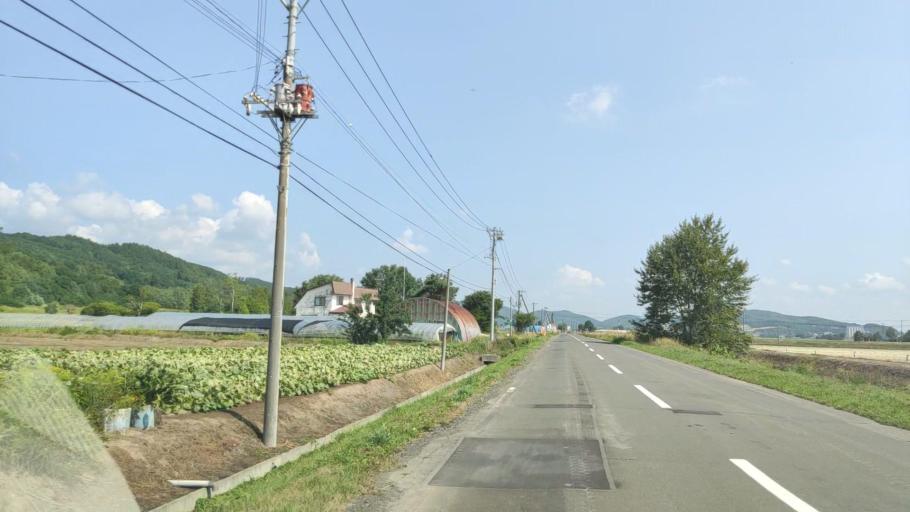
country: JP
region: Hokkaido
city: Shimo-furano
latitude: 43.3790
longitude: 142.3906
